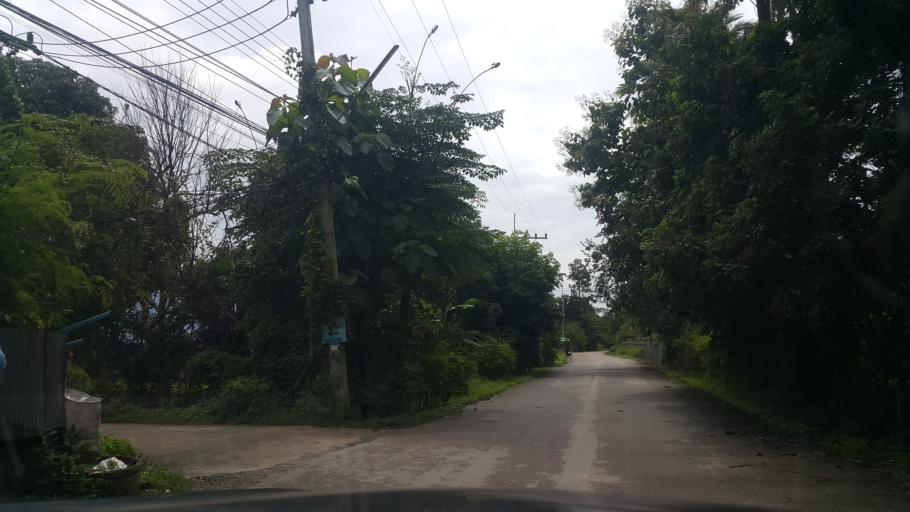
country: TH
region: Chiang Mai
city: San Sai
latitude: 18.9063
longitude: 99.0533
